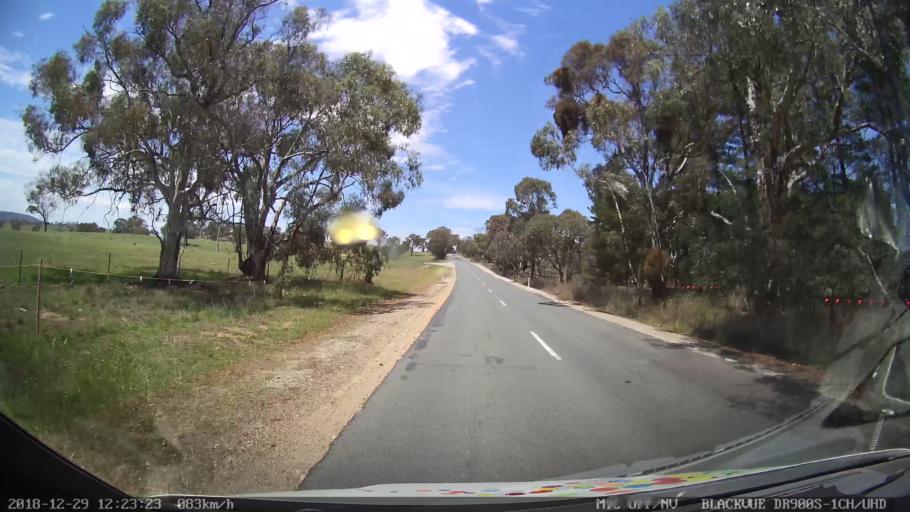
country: AU
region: New South Wales
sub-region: Queanbeyan
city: Queanbeyan
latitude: -35.4355
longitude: 149.2165
